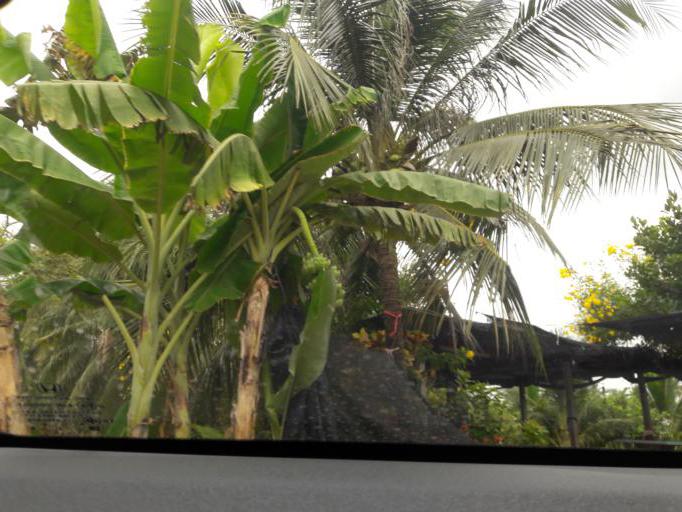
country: TH
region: Ratchaburi
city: Damnoen Saduak
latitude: 13.5631
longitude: 99.9981
